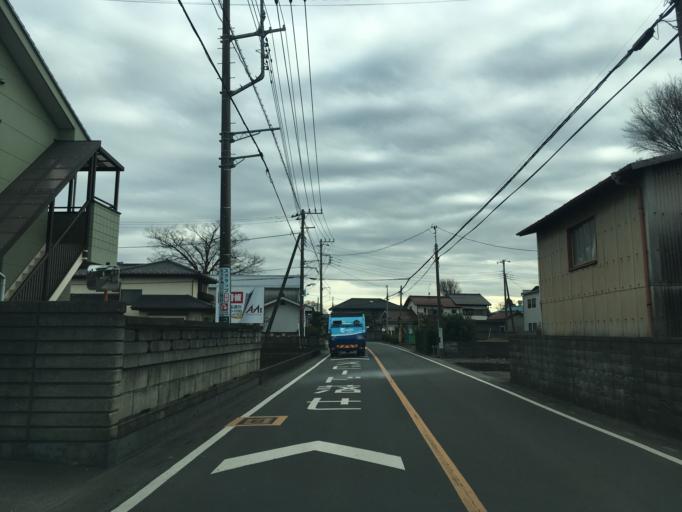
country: JP
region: Saitama
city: Sayama
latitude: 35.7945
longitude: 139.3988
